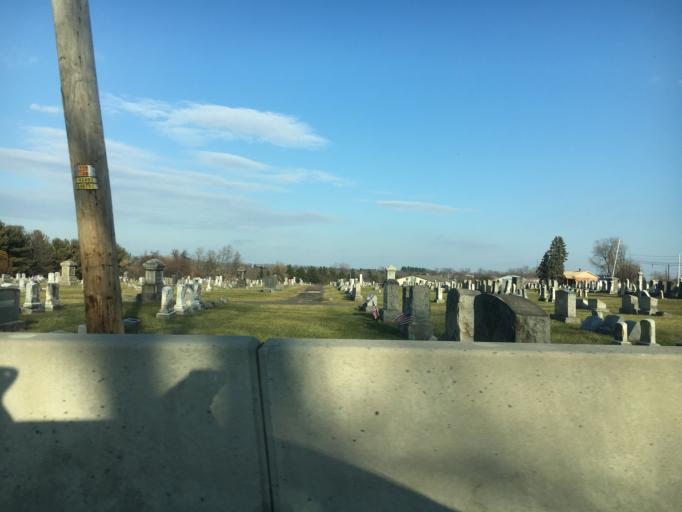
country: US
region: Pennsylvania
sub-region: Lehigh County
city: Hokendauqua
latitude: 40.6495
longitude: -75.4987
